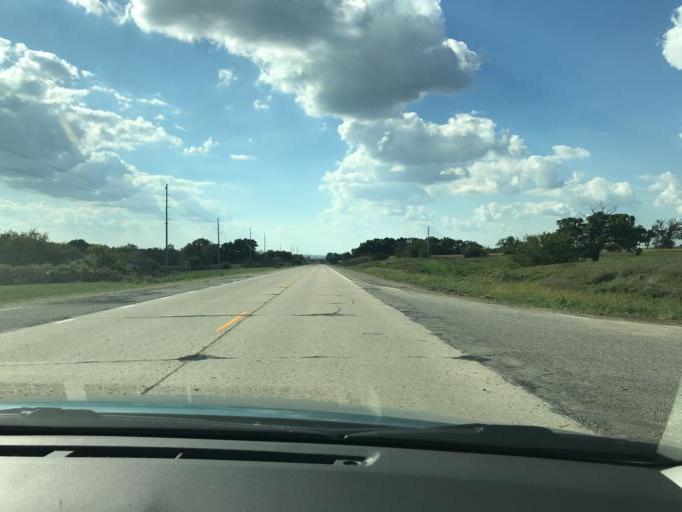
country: US
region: Wisconsin
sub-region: Rock County
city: Orfordville
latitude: 42.5582
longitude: -89.3066
